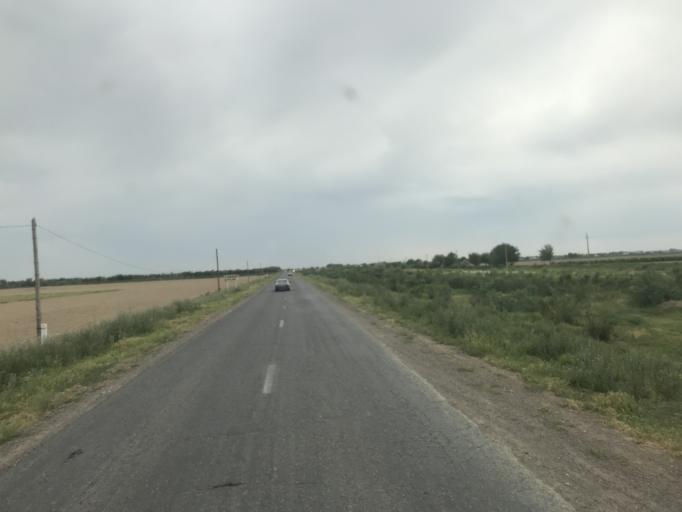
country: KZ
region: Ongtustik Qazaqstan
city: Asykata
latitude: 40.9246
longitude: 68.4026
